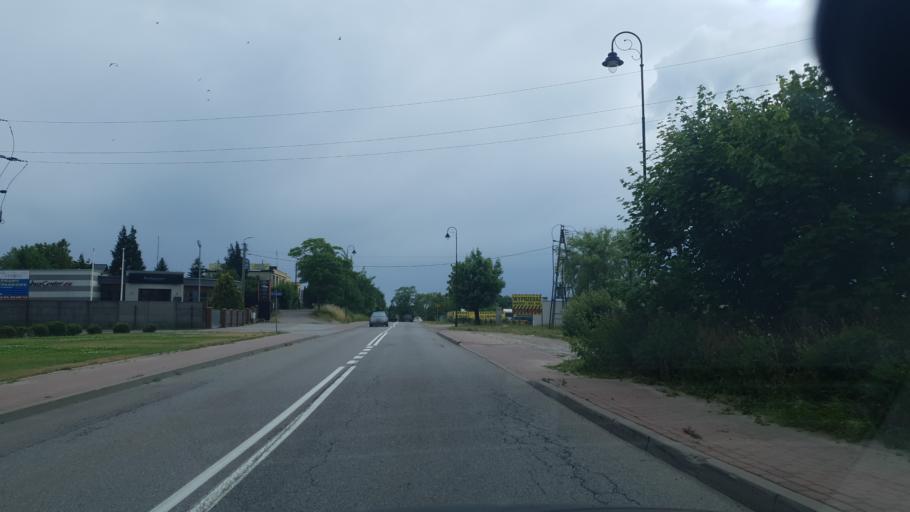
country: PL
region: Pomeranian Voivodeship
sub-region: Powiat kartuski
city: Przodkowo
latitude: 54.3754
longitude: 18.2834
